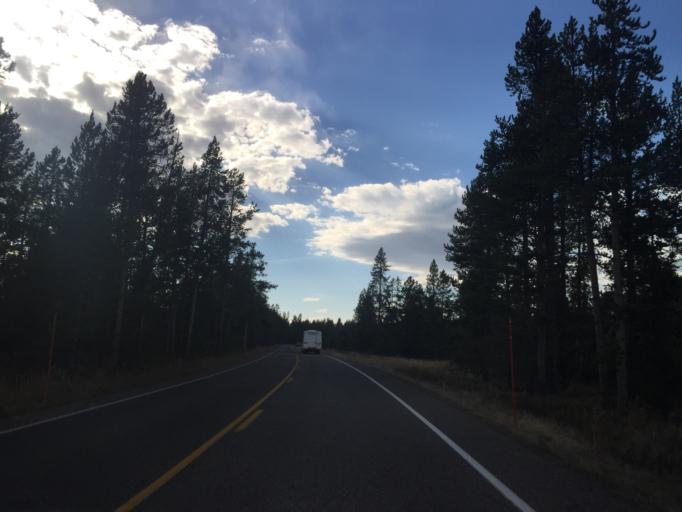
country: US
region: Montana
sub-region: Gallatin County
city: West Yellowstone
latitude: 44.6536
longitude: -111.0656
